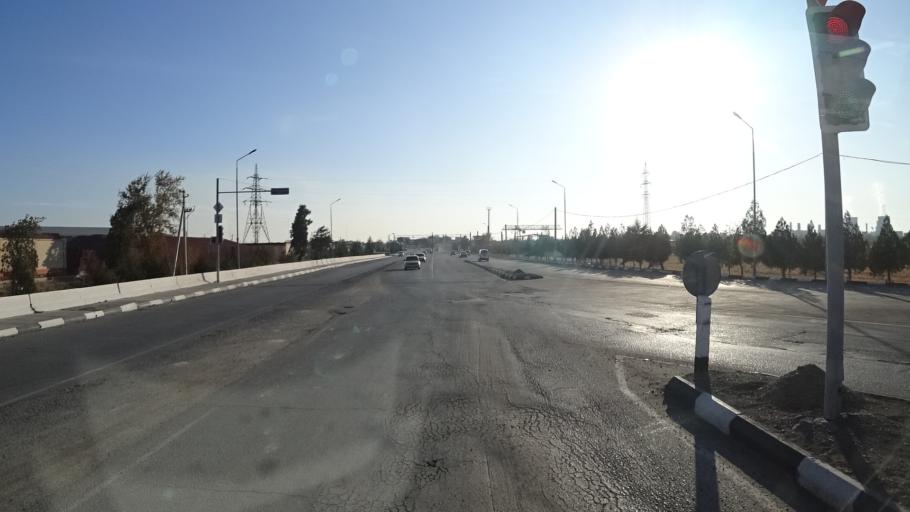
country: UZ
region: Navoiy
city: Beshrabot
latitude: 40.1647
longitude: 65.3311
